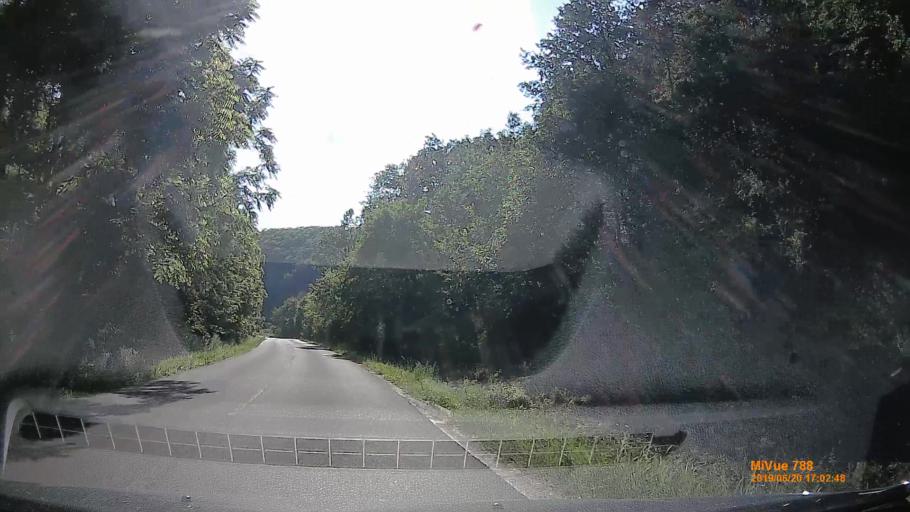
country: HU
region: Baranya
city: Buekkoesd
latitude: 46.1287
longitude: 18.0159
